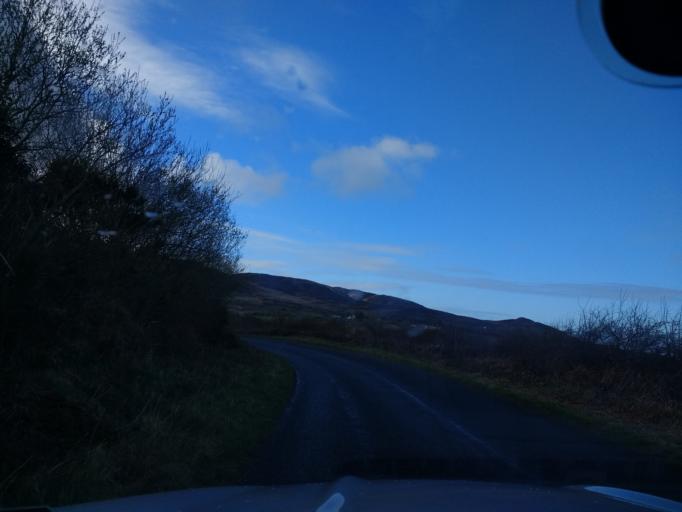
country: IE
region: Ulster
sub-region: County Donegal
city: Buncrana
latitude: 55.1650
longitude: -7.5702
